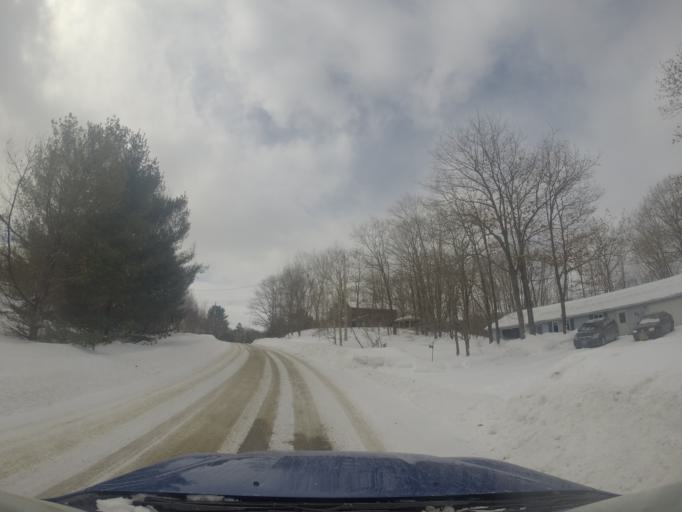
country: CA
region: Ontario
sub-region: Parry Sound District
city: Parry Sound
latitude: 45.3870
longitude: -80.0277
